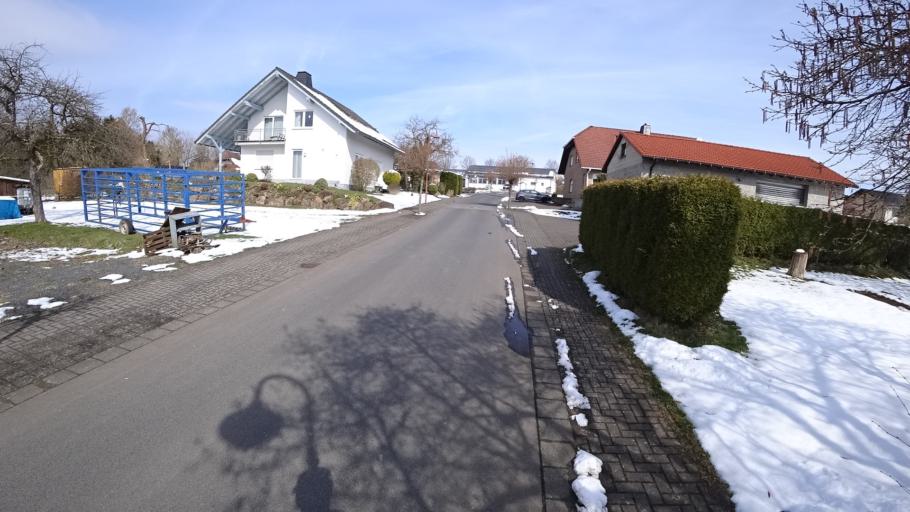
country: DE
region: Rheinland-Pfalz
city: Morlen
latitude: 50.6975
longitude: 7.8867
